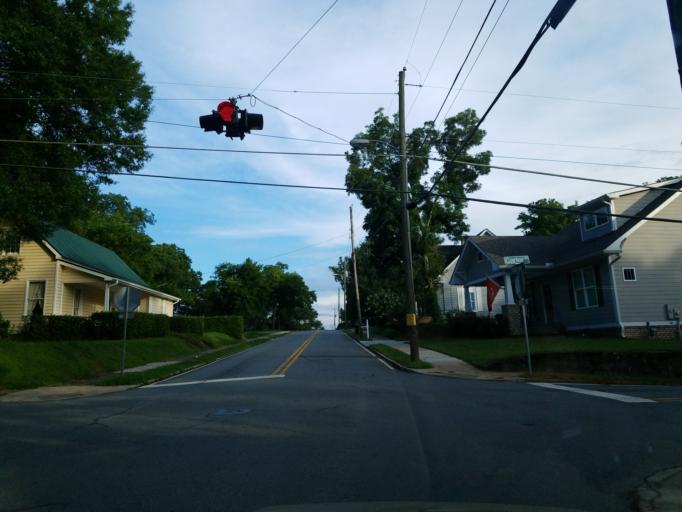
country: US
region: Georgia
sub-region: Bartow County
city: Cartersville
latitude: 34.1711
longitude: -84.7965
